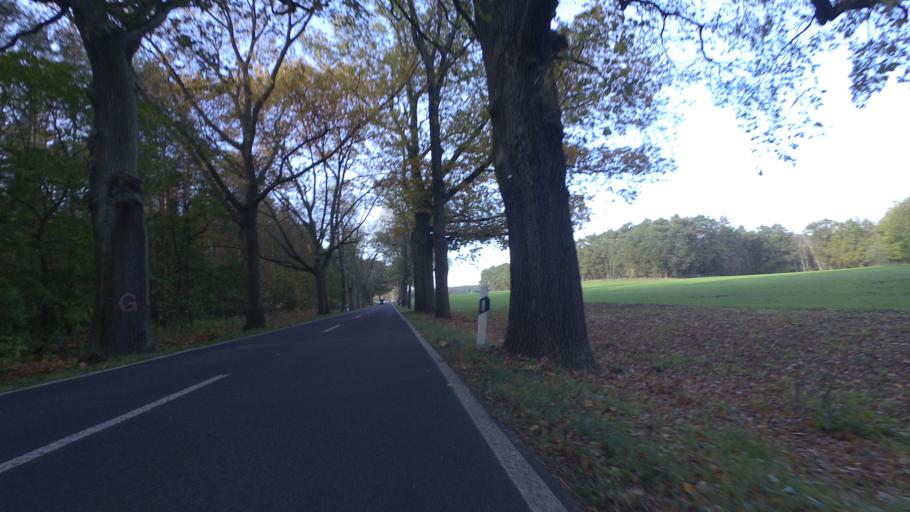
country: DE
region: Brandenburg
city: Sperenberg
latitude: 52.1936
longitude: 13.3176
